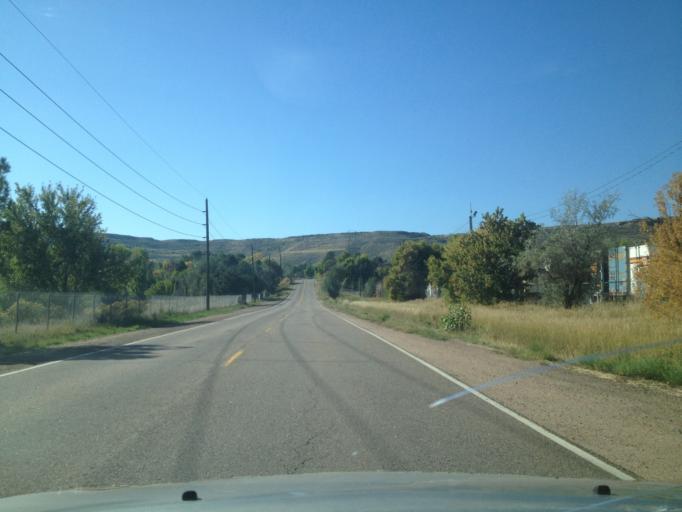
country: US
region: Colorado
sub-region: Jefferson County
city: Applewood
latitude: 39.7652
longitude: -105.1748
